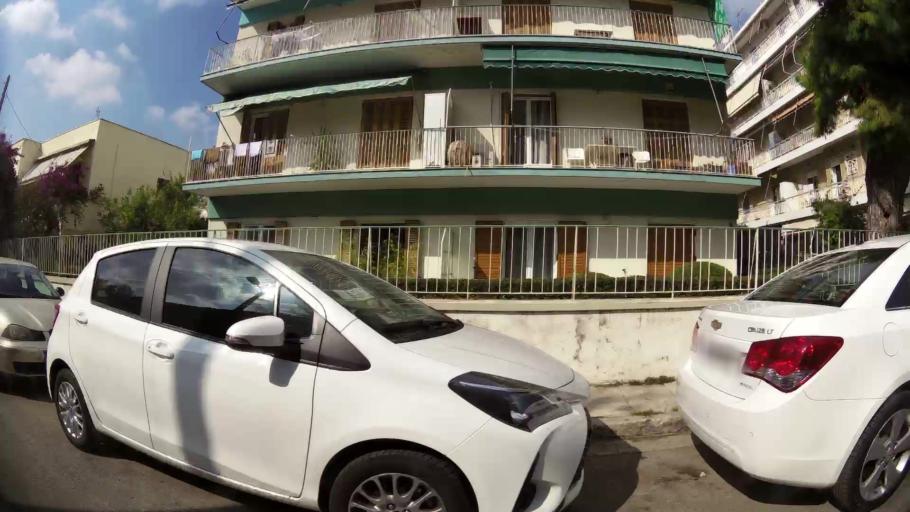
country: GR
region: Attica
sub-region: Nomarchia Athinas
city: Cholargos
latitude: 38.0008
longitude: 23.7989
